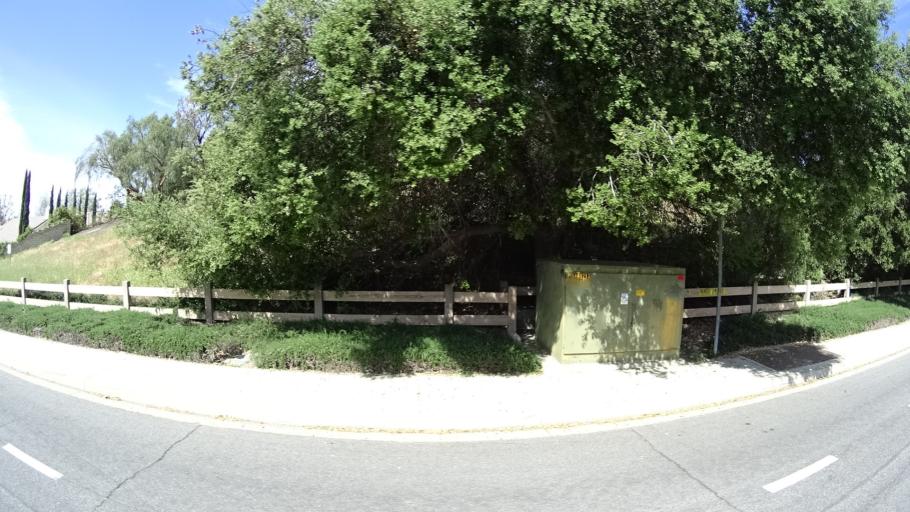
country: US
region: California
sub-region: Ventura County
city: Thousand Oaks
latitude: 34.2133
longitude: -118.8357
